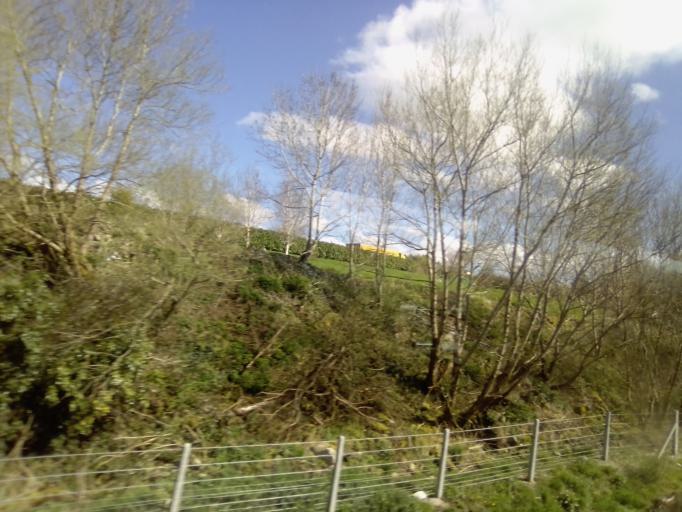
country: IE
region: Munster
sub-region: Ciarrai
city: Cill Airne
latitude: 52.0994
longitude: -9.5189
